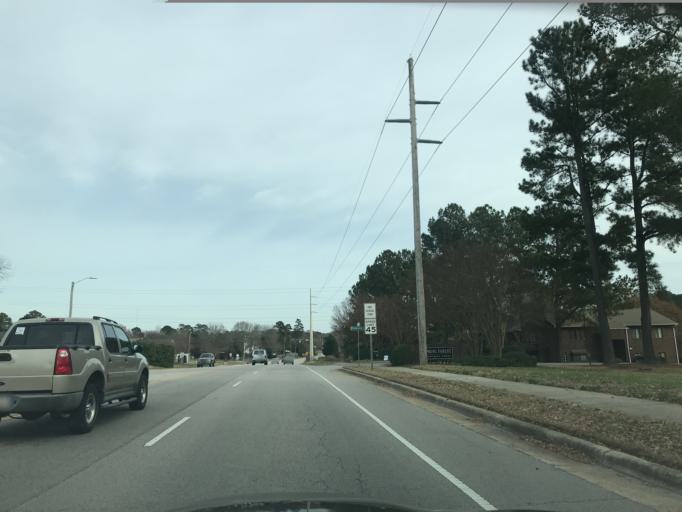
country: US
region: North Carolina
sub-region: Wake County
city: Raleigh
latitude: 35.8557
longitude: -78.5741
